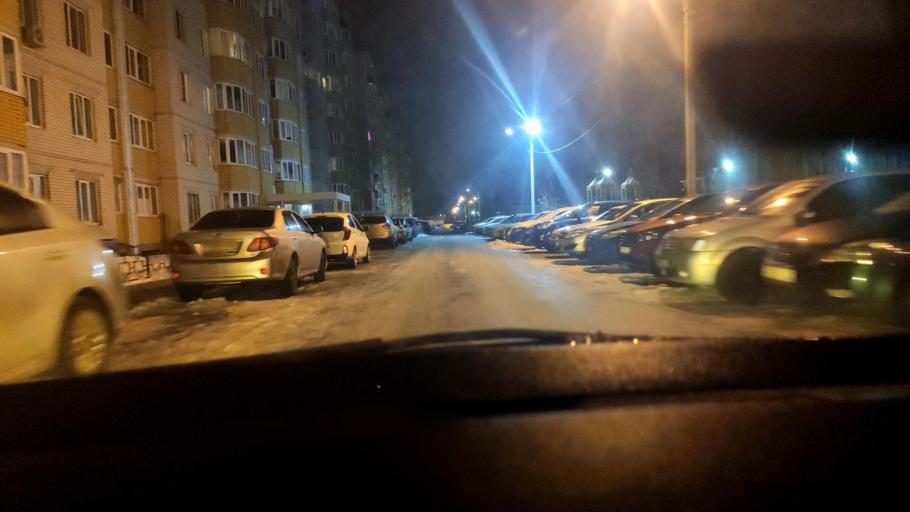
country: RU
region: Voronezj
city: Somovo
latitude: 51.7392
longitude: 39.3188
